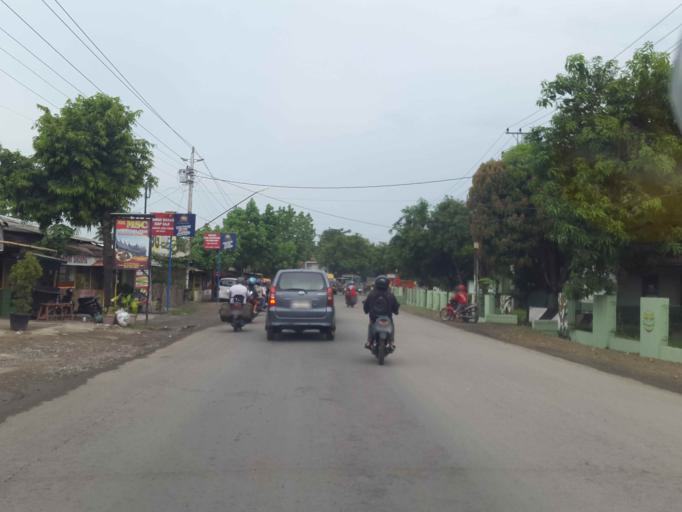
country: ID
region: Central Java
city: Adiwerna
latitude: -6.9431
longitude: 109.1243
